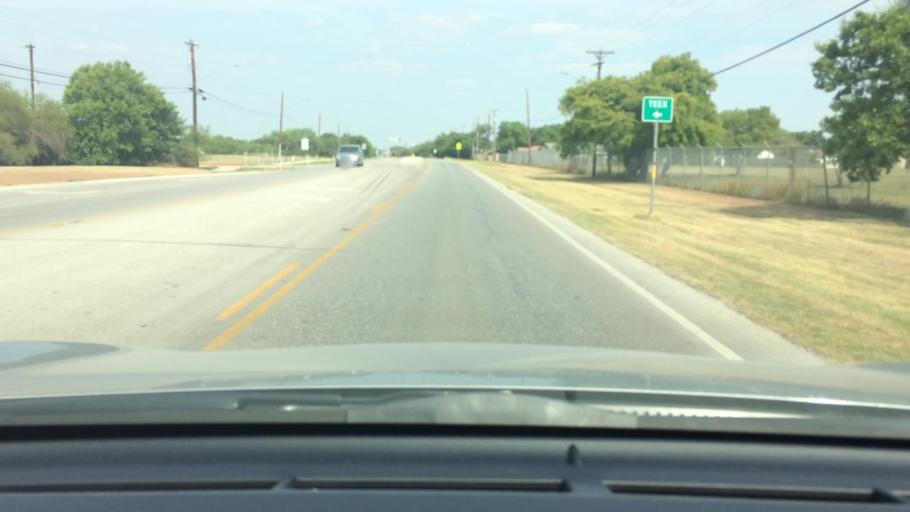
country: US
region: Texas
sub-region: Bexar County
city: China Grove
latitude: 29.3286
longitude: -98.4397
